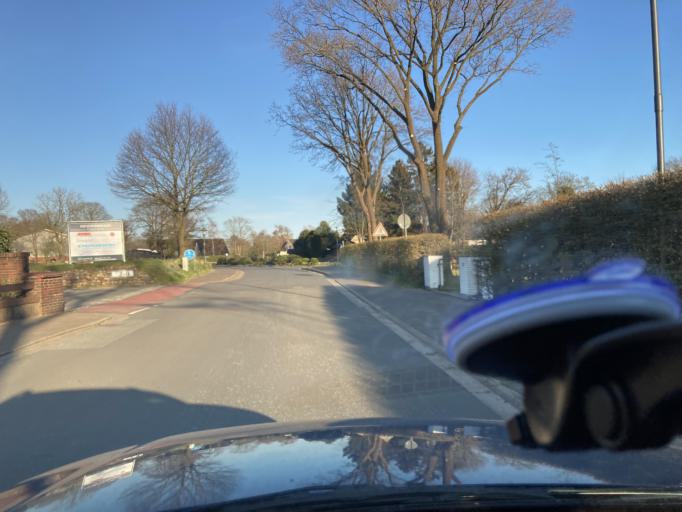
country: DE
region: Schleswig-Holstein
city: Suderheistedt
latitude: 54.2143
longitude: 9.1297
